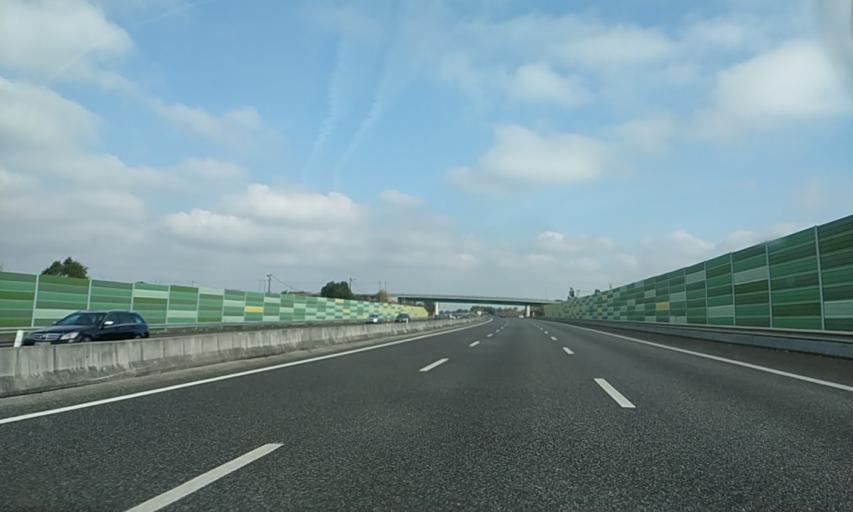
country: PT
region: Santarem
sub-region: Cartaxo
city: Pontevel
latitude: 39.1762
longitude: -8.8375
